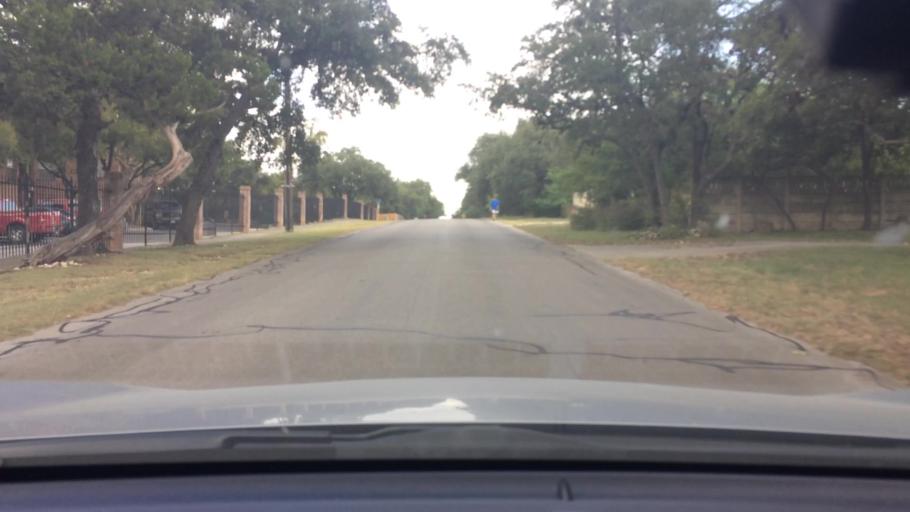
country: US
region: Texas
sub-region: Bexar County
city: Hollywood Park
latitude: 29.5579
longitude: -98.4703
